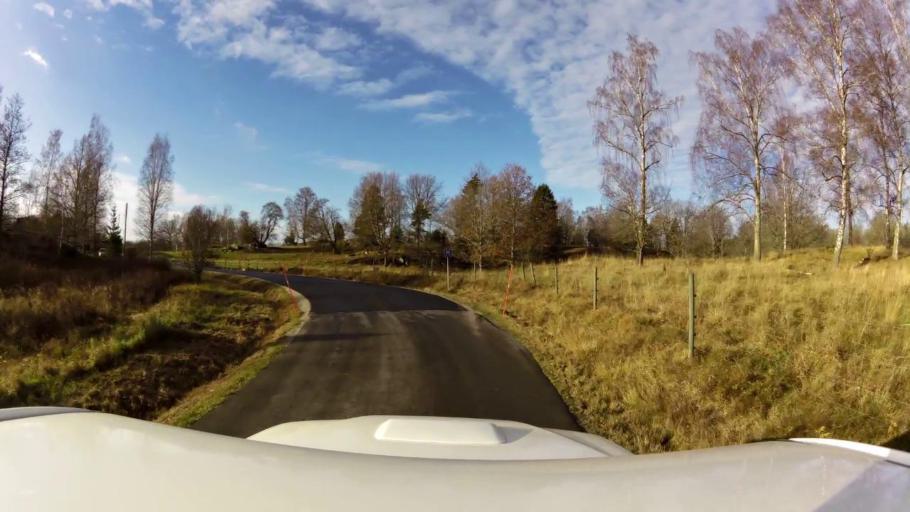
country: SE
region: OEstergoetland
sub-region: Linkopings Kommun
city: Sturefors
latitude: 58.2633
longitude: 15.6751
